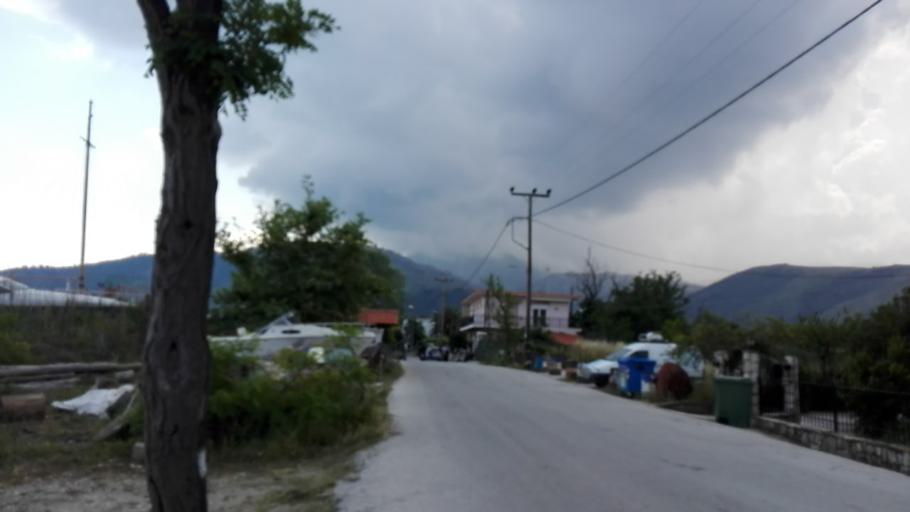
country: GR
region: East Macedonia and Thrace
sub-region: Nomos Kavalas
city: Prinos
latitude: 40.7593
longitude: 24.5733
